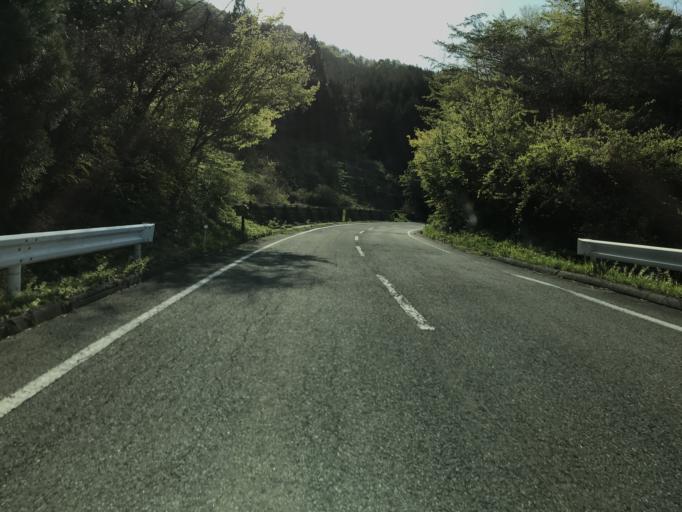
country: JP
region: Fukushima
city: Funehikimachi-funehiki
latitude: 37.5424
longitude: 140.7371
